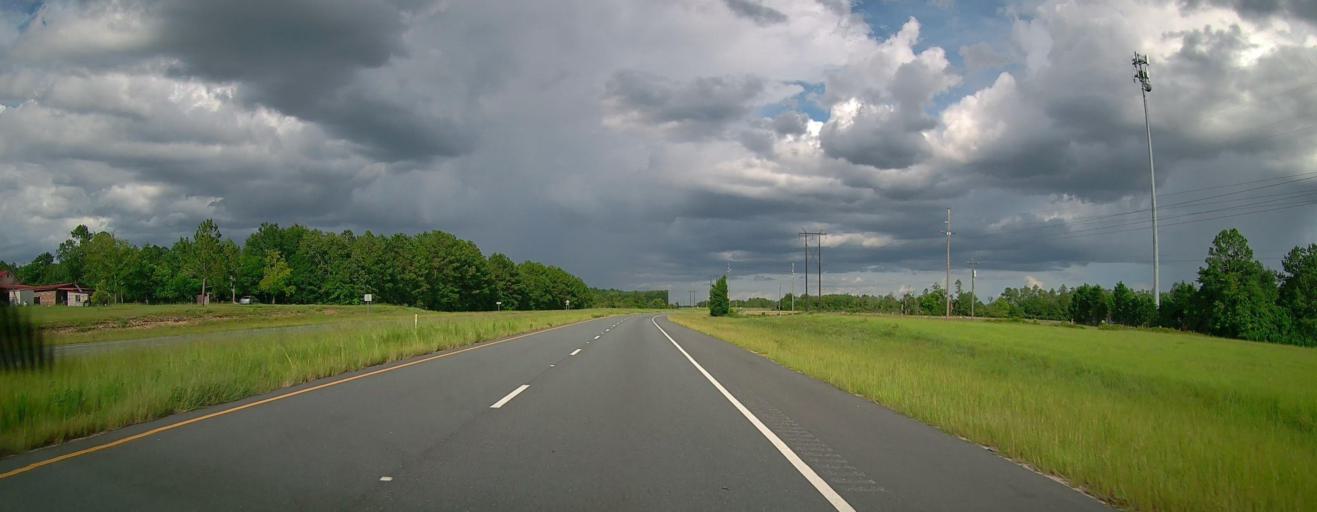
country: US
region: Georgia
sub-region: Taylor County
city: Butler
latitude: 32.5924
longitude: -84.3857
